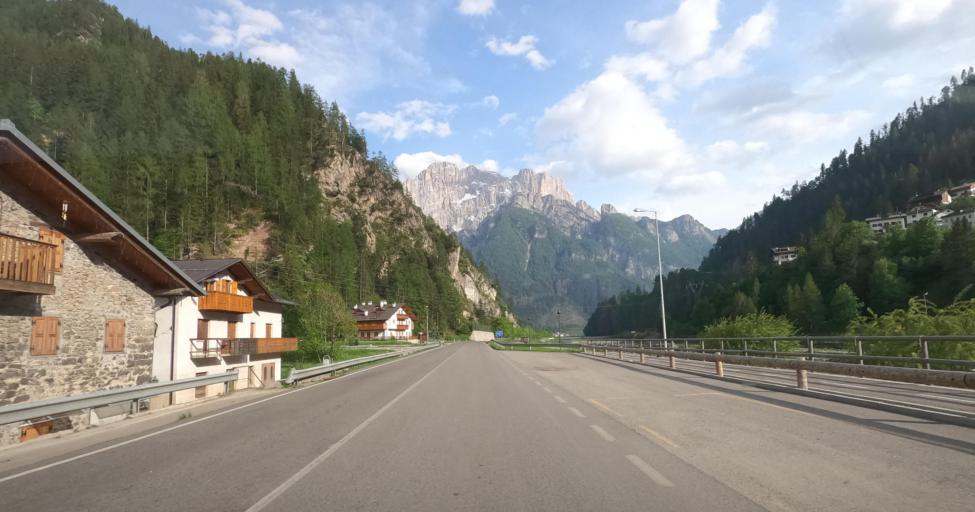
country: IT
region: Veneto
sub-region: Provincia di Belluno
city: Alleghe
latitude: 46.4222
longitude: 12.0093
